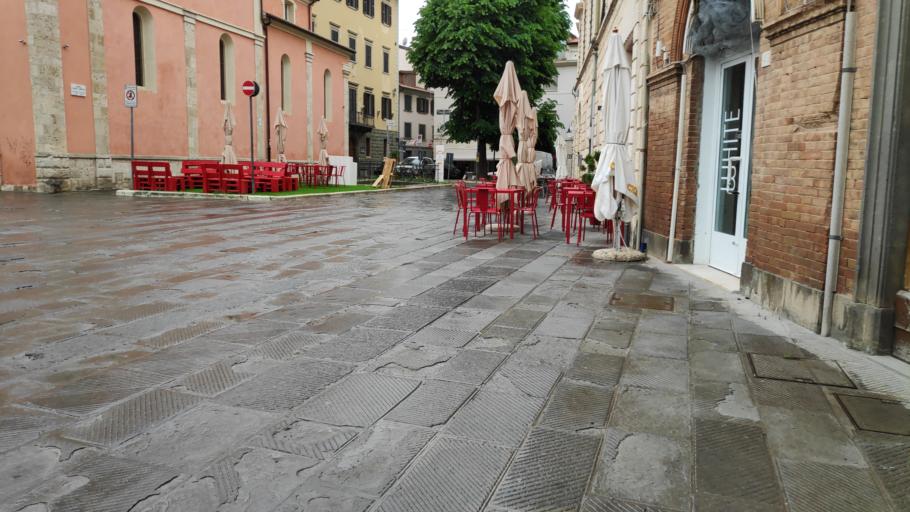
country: IT
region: Tuscany
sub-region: Provincia di Grosseto
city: Grosseto
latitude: 42.7610
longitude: 11.1156
